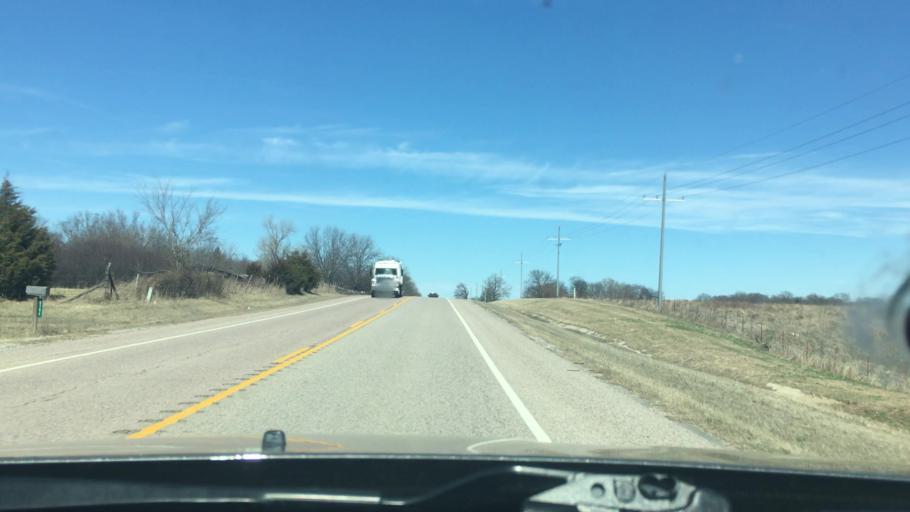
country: US
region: Oklahoma
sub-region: Murray County
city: Sulphur
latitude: 34.4132
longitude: -96.9508
